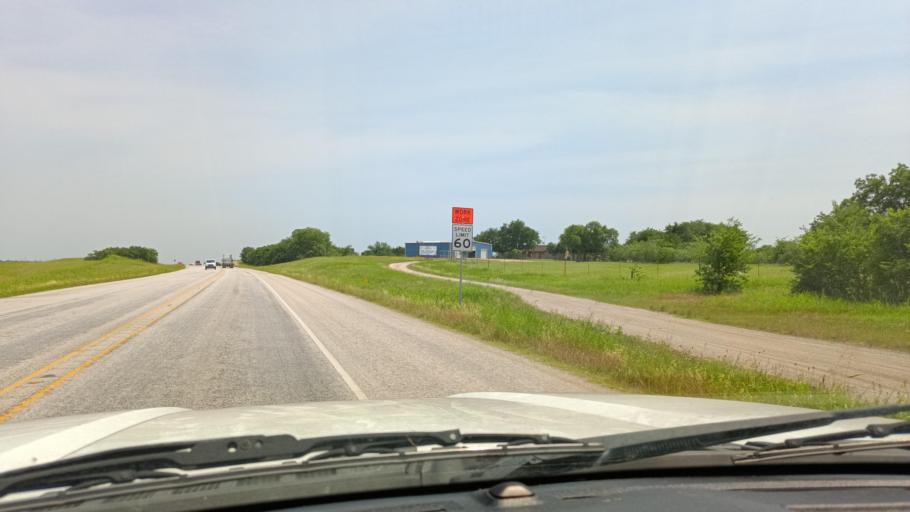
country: US
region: Texas
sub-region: Bell County
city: Rogers
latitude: 30.9518
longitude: -97.2537
